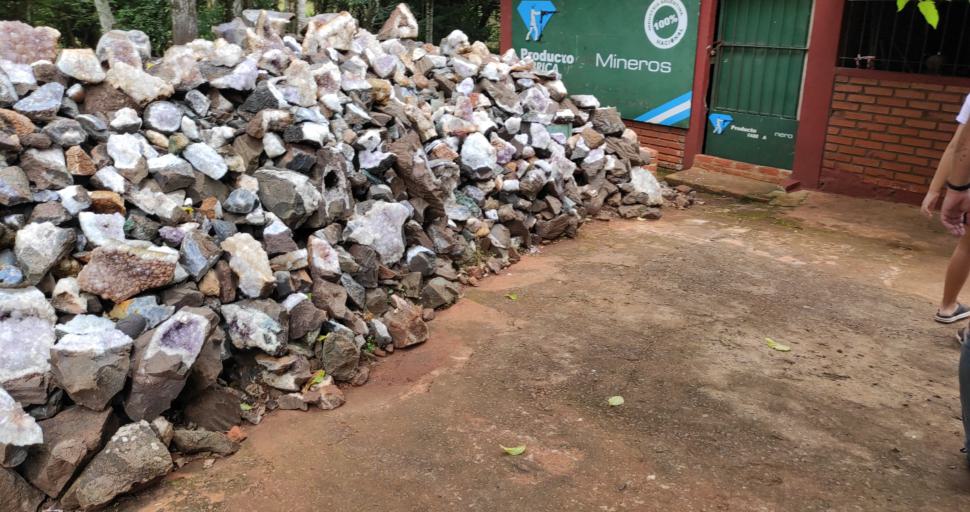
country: AR
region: Misiones
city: Puerto Libertad
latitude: -25.9574
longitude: -54.5990
